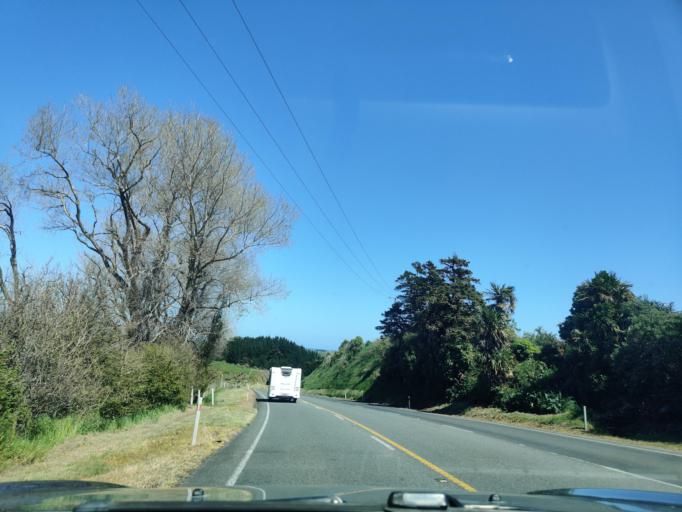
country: NZ
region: Taranaki
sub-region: South Taranaki District
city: Patea
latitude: -39.8099
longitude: 174.7473
